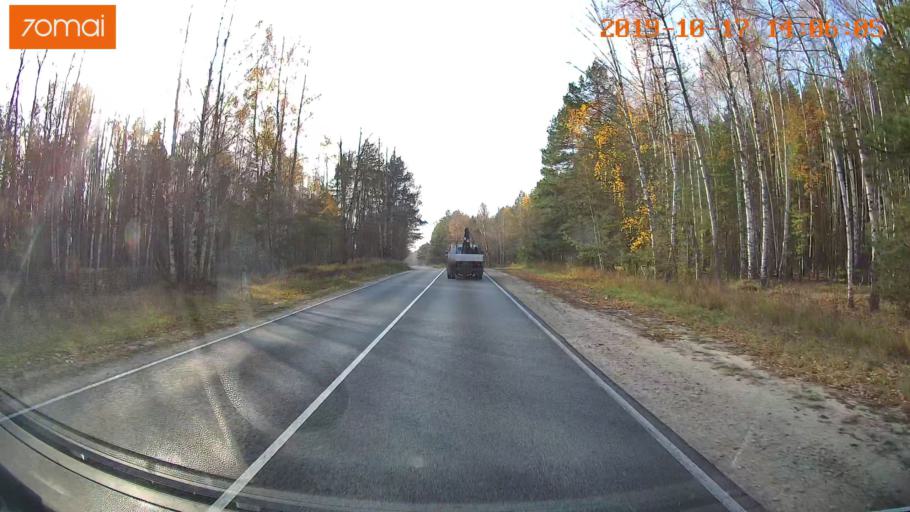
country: RU
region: Rjazan
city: Spas-Klepiki
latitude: 55.1148
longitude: 40.1127
